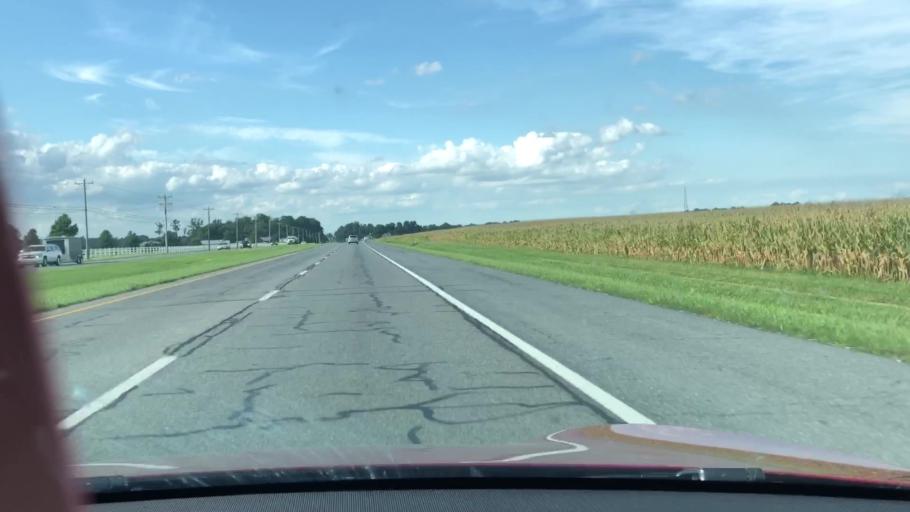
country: US
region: Delaware
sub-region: Kent County
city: Harrington
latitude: 38.9556
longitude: -75.5644
